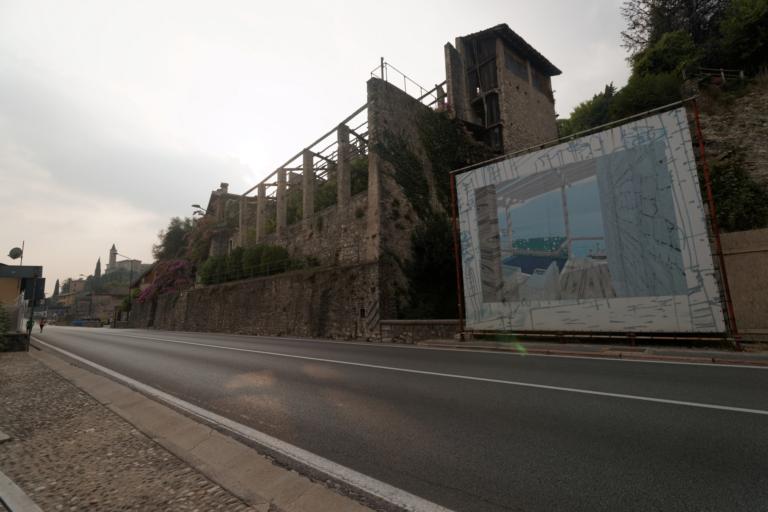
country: IT
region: Lombardy
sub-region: Provincia di Brescia
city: Gargnano
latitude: 45.6858
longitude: 10.6597
